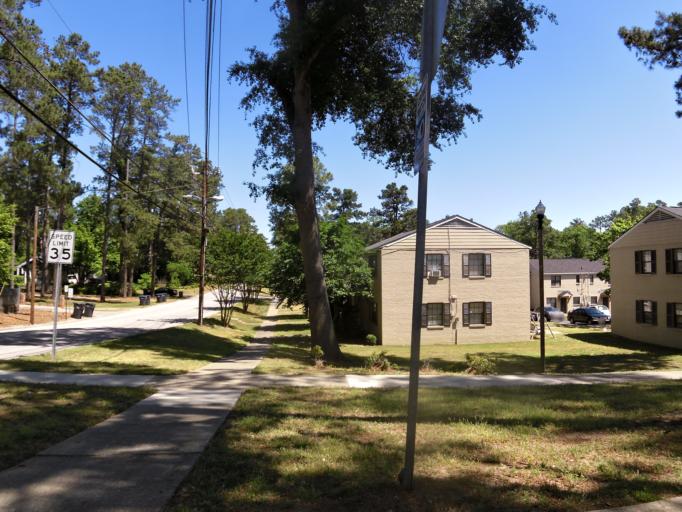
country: US
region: Georgia
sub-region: Columbia County
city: Martinez
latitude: 33.4813
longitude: -82.0395
